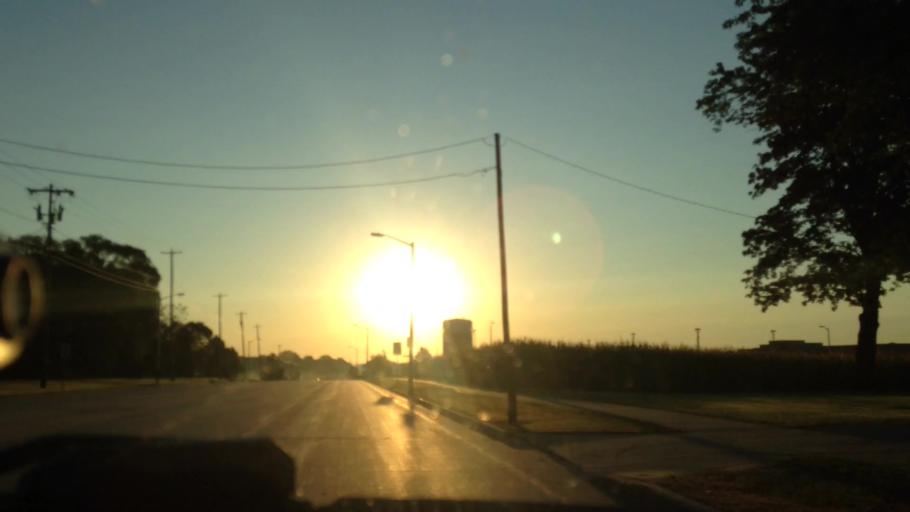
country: US
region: Wisconsin
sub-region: Washington County
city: West Bend
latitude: 43.4266
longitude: -88.1483
